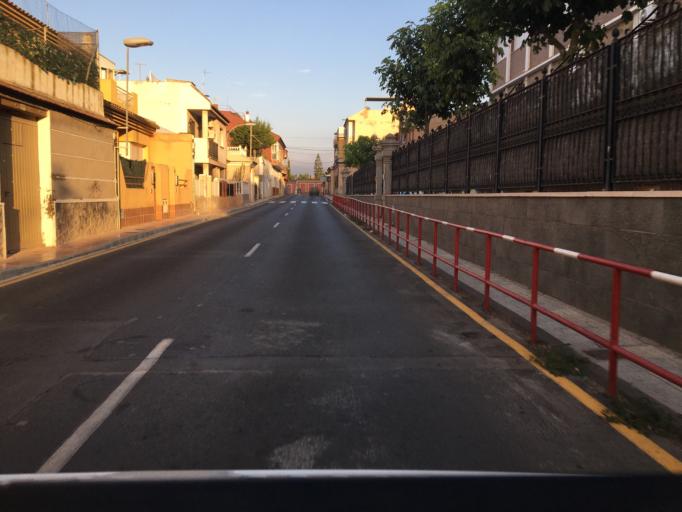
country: ES
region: Murcia
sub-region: Murcia
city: Cartagena
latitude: 37.6238
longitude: -0.9870
